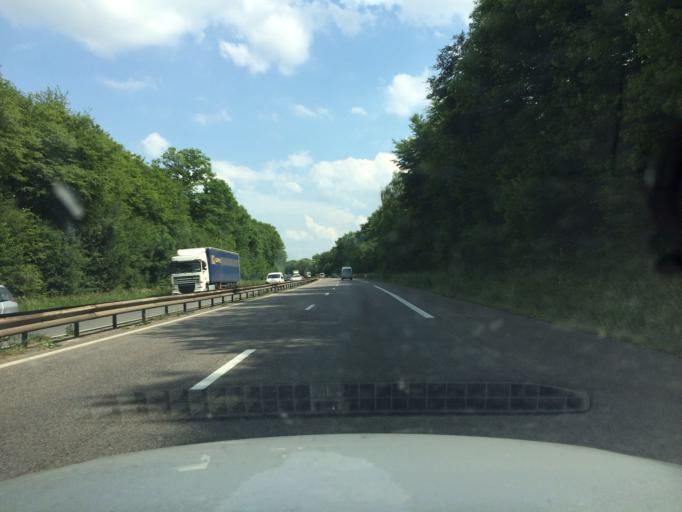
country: FR
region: Lorraine
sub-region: Departement de Meurthe-et-Moselle
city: Chavigny
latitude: 48.6524
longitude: 6.1299
